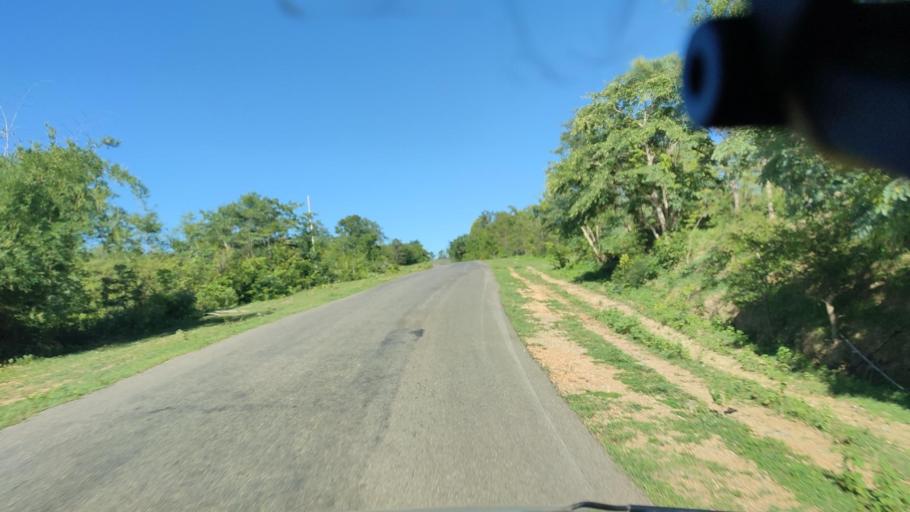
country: MM
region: Magway
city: Magway
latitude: 19.7519
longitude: 94.9466
